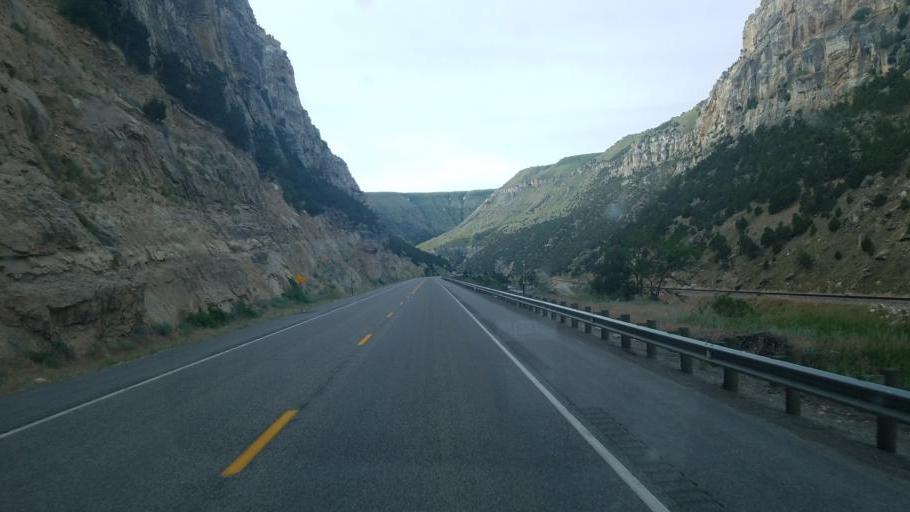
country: US
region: Wyoming
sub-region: Hot Springs County
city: Thermopolis
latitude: 43.5684
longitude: -108.2102
